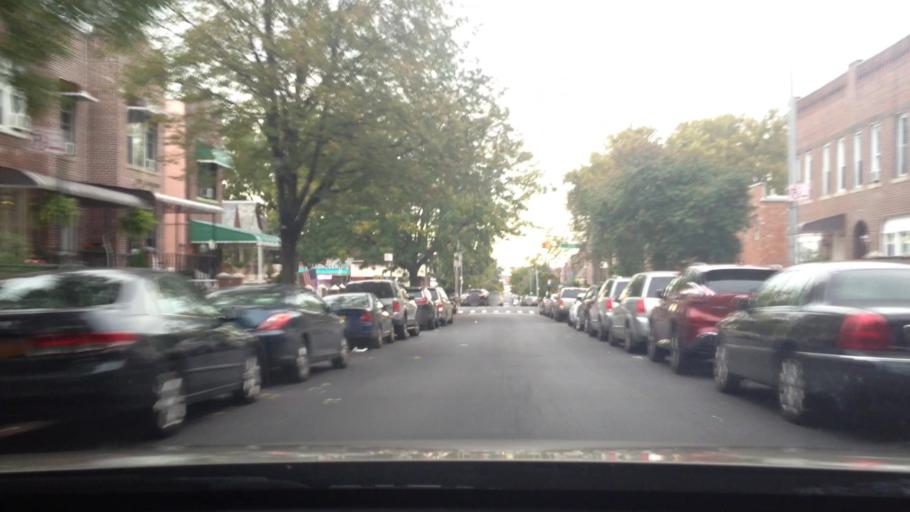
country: US
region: New York
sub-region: Queens County
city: Long Island City
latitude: 40.7592
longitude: -73.8794
